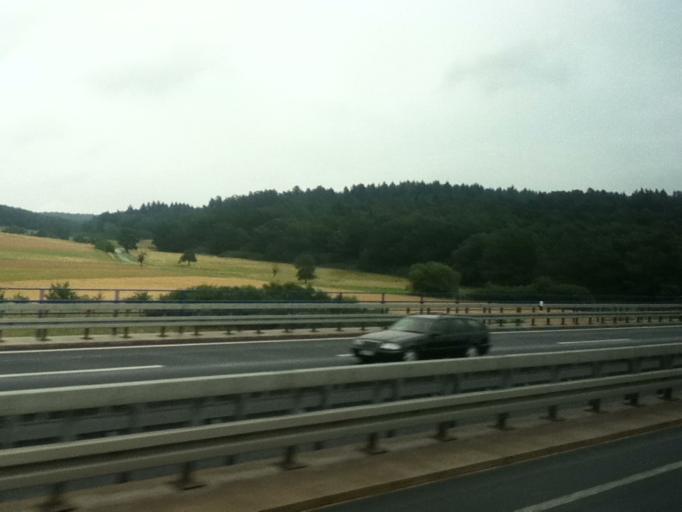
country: DE
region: Hesse
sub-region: Regierungsbezirk Giessen
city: Sinn
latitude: 50.6242
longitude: 8.3539
